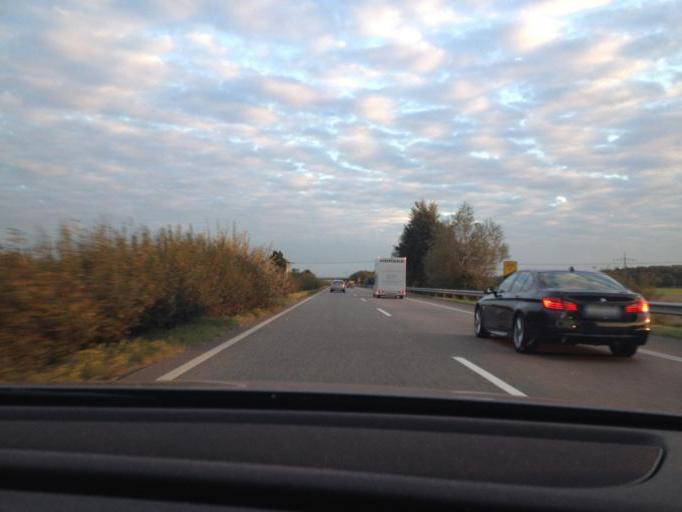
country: DE
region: Rheinland-Pfalz
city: Waldsee
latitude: 49.3944
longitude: 8.4142
